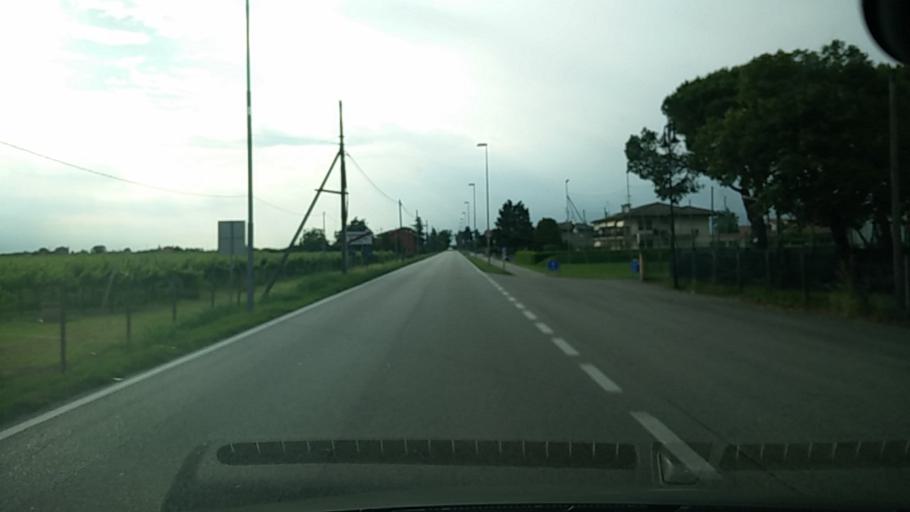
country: IT
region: Veneto
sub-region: Provincia di Venezia
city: Passarella
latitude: 45.5703
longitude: 12.6230
